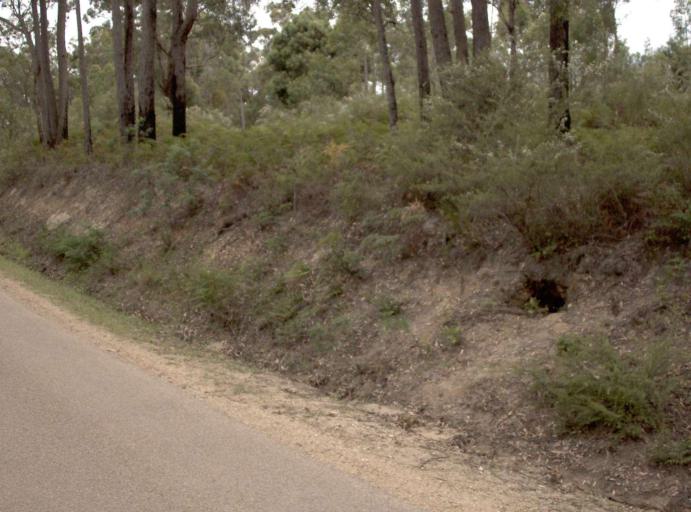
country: AU
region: Victoria
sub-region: East Gippsland
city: Bairnsdale
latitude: -37.7474
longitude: 147.5975
